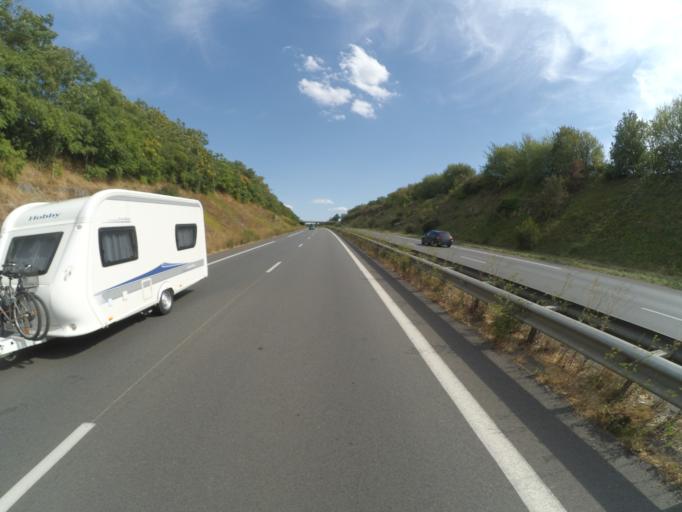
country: FR
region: Poitou-Charentes
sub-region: Departement de la Vienne
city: Migne-Auxances
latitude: 46.6236
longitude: 0.3007
